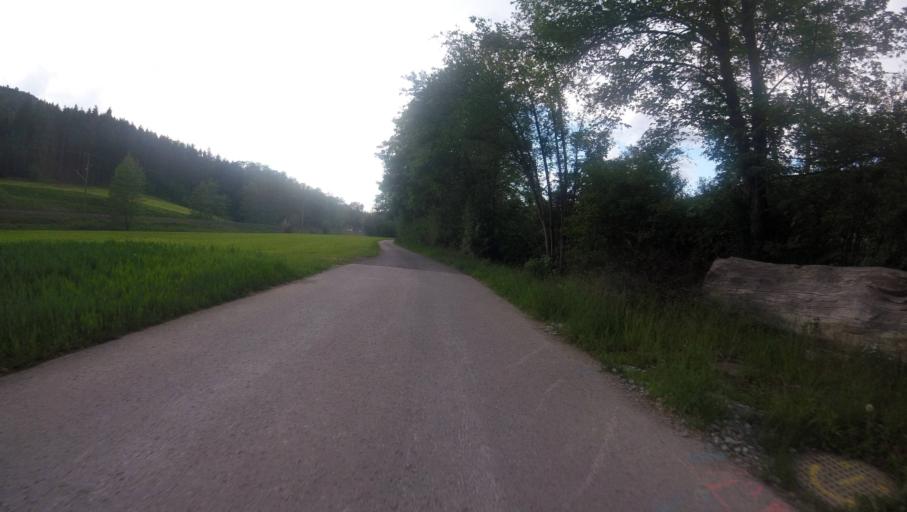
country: DE
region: Baden-Wuerttemberg
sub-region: Regierungsbezirk Stuttgart
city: Sulzbach an der Murr
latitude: 48.9959
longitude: 9.5285
